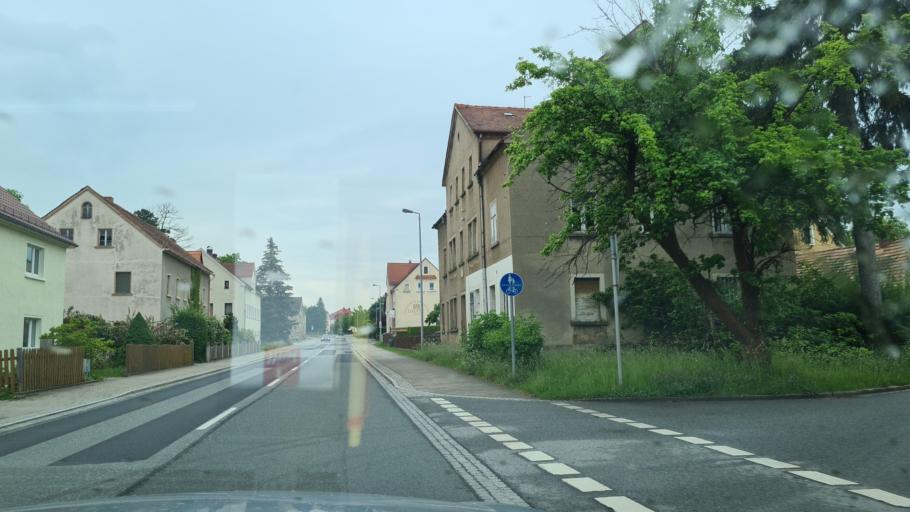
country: DE
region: Saxony
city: Grosspostwitz
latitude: 51.1159
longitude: 14.4417
